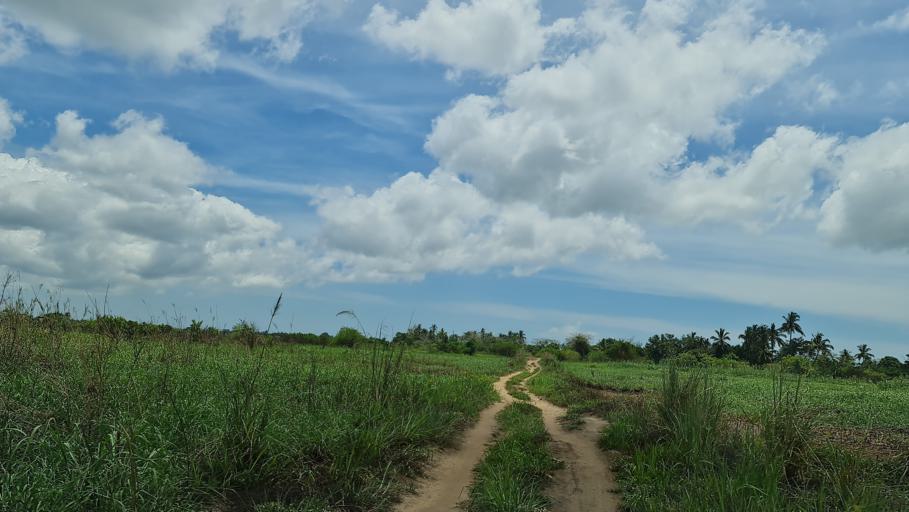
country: MZ
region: Zambezia
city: Quelimane
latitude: -17.5827
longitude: 37.3777
